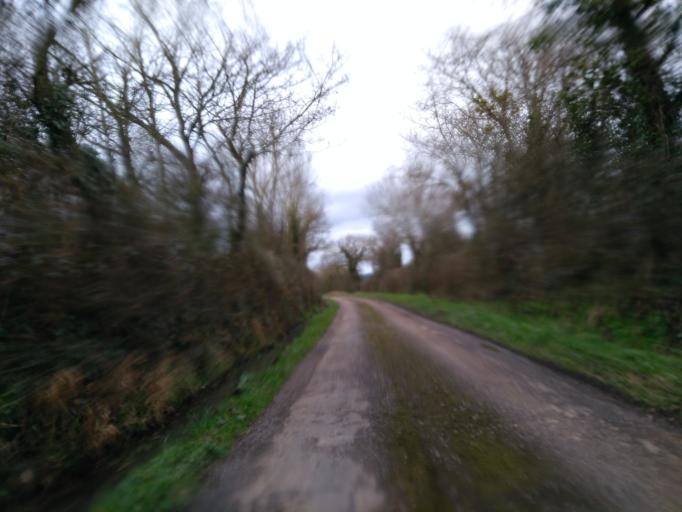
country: GB
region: England
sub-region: Devon
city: Heavitree
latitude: 50.7936
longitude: -3.5010
